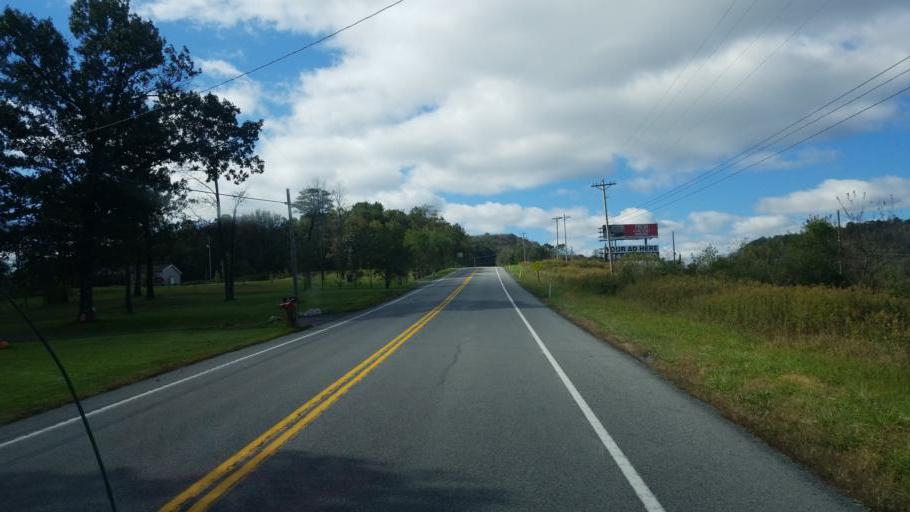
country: US
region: Pennsylvania
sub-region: Bedford County
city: Earlston
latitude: 40.0174
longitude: -78.1915
